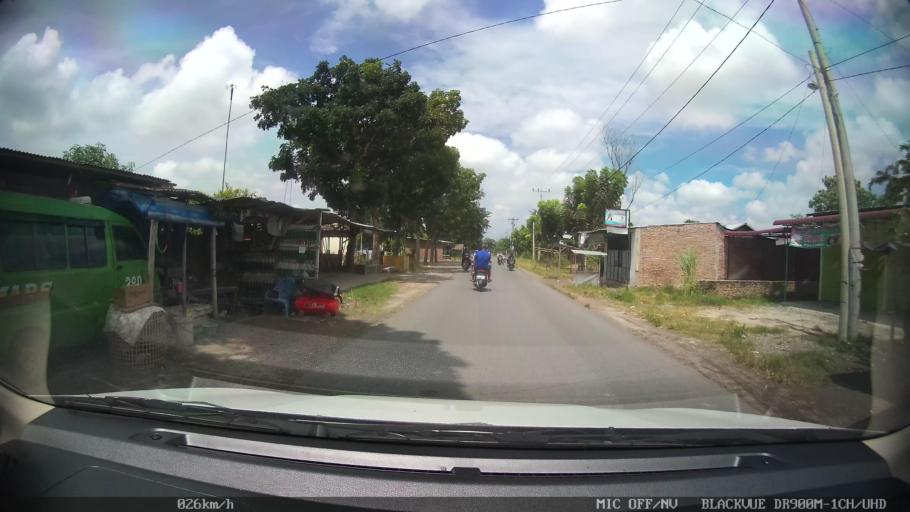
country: ID
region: North Sumatra
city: Percut
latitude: 3.6197
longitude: 98.7801
